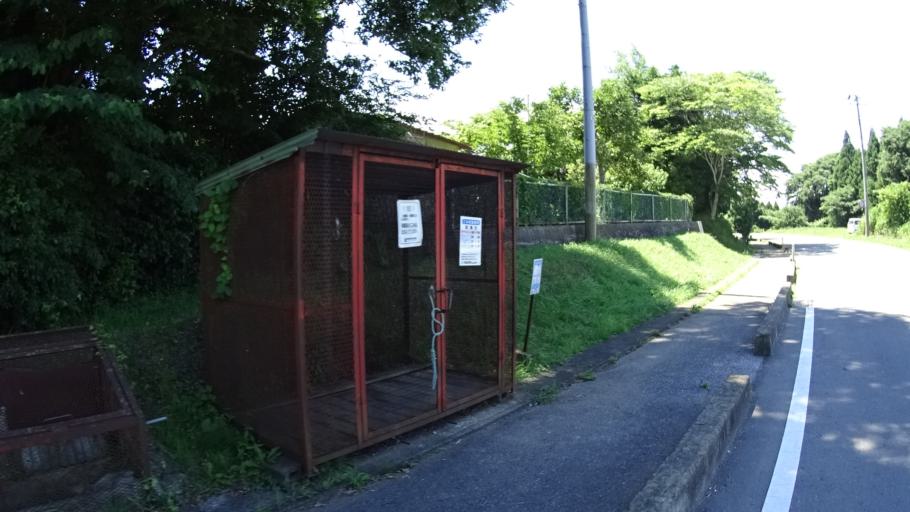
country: JP
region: Iwate
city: Ofunato
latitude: 38.8407
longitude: 141.6250
